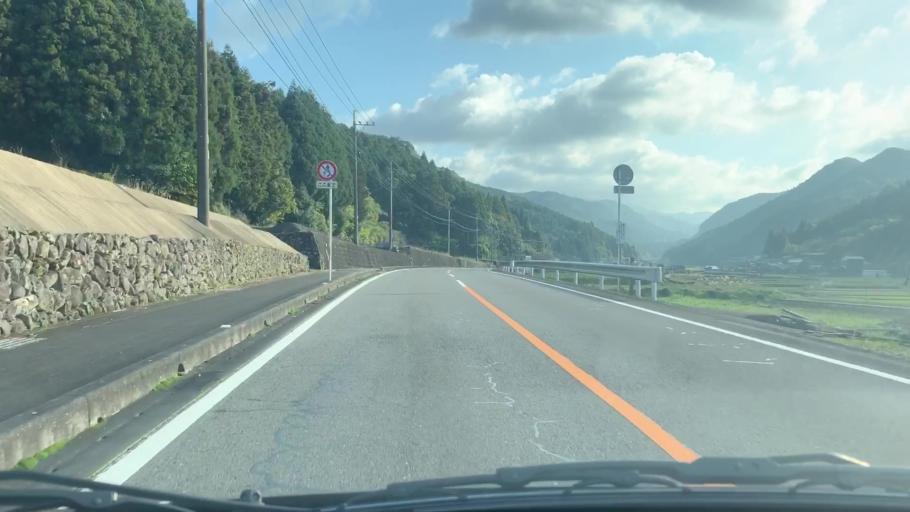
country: JP
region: Saga Prefecture
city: Kashima
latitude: 33.0699
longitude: 130.0698
